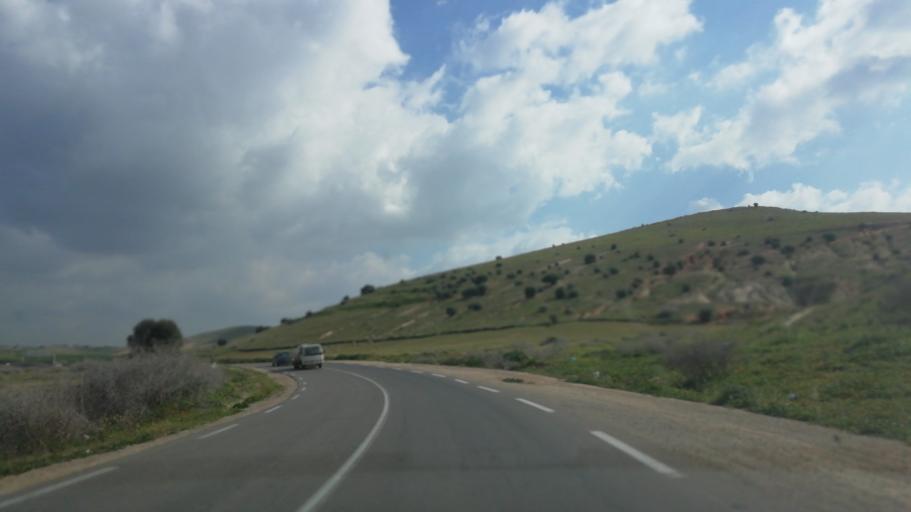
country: DZ
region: Mostaganem
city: Mostaganem
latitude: 35.7026
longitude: 0.2303
